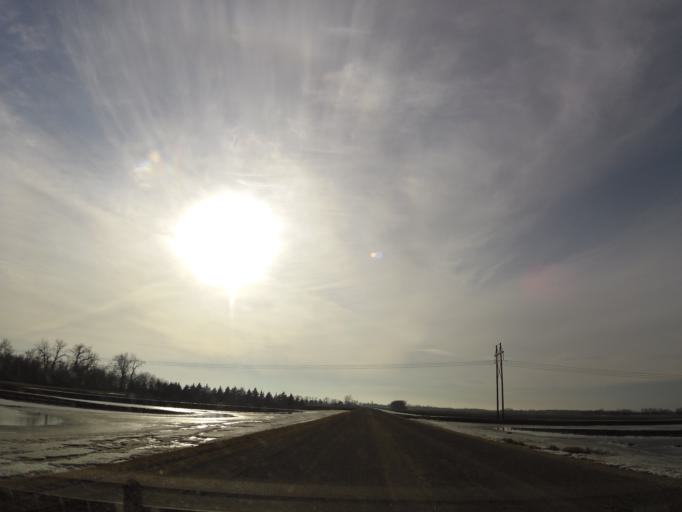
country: US
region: North Dakota
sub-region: Walsh County
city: Grafton
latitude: 48.4266
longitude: -97.2650
